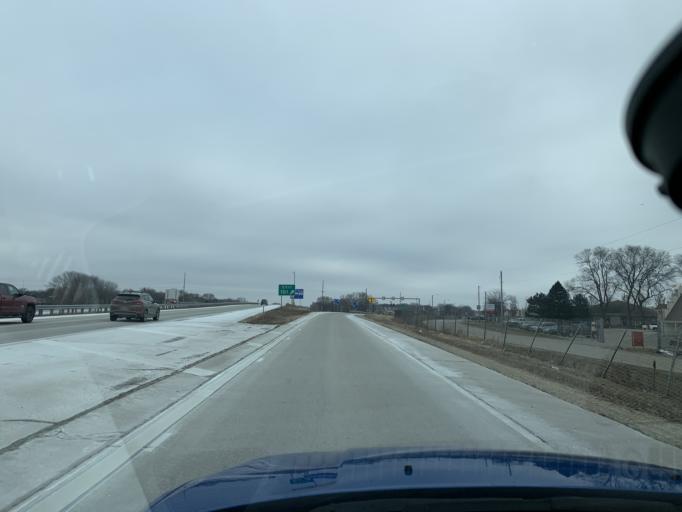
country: US
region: Wisconsin
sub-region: Dane County
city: Sun Prairie
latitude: 43.1740
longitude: -89.2518
